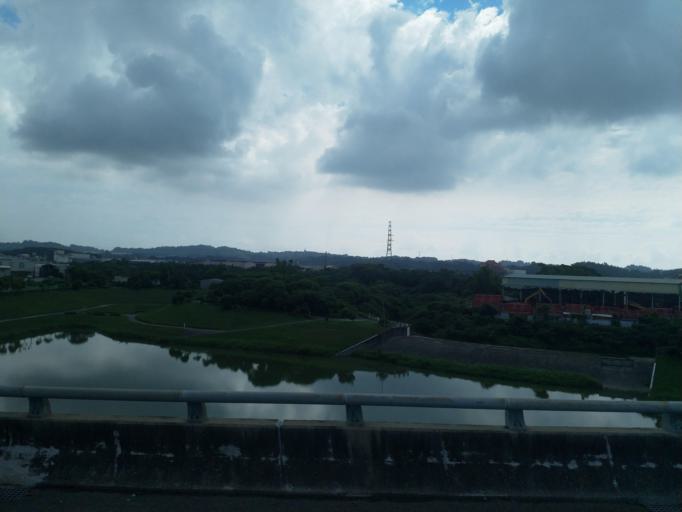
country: TW
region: Taiwan
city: Fengshan
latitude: 22.6934
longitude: 120.3580
